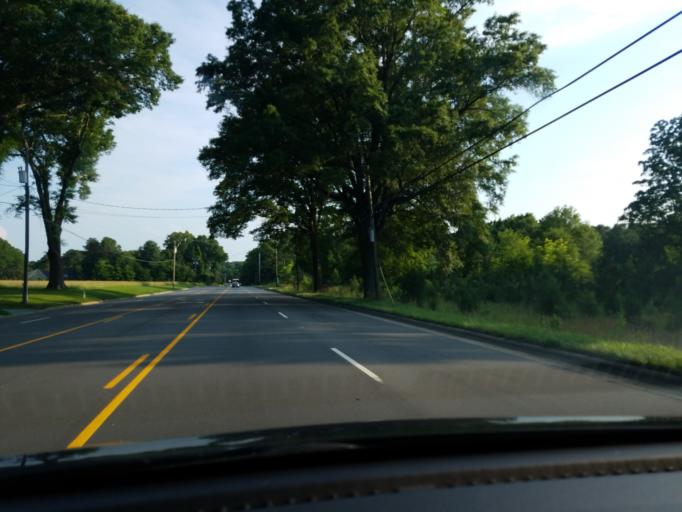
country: US
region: North Carolina
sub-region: Durham County
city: Gorman
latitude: 36.1071
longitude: -78.9090
